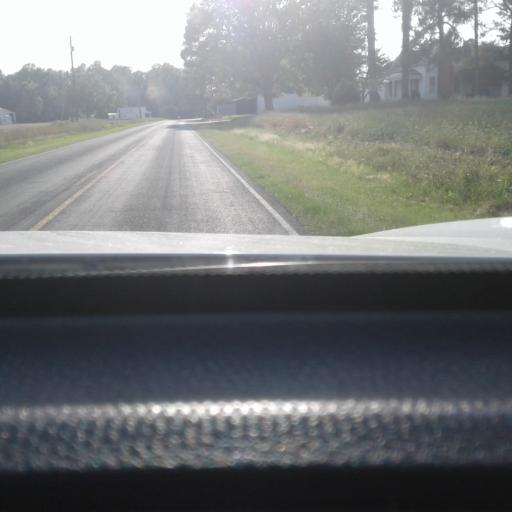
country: US
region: North Carolina
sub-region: Harnett County
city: Dunn
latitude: 35.3348
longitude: -78.5815
